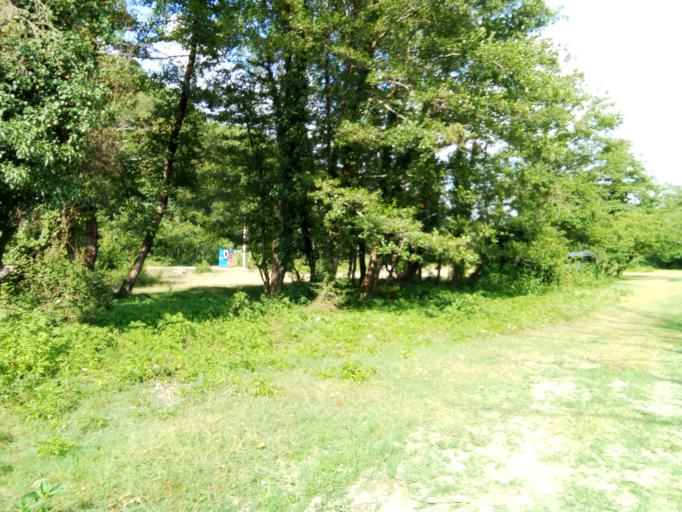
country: RU
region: Krasnodarskiy
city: Vardane
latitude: 43.8399
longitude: 39.5300
